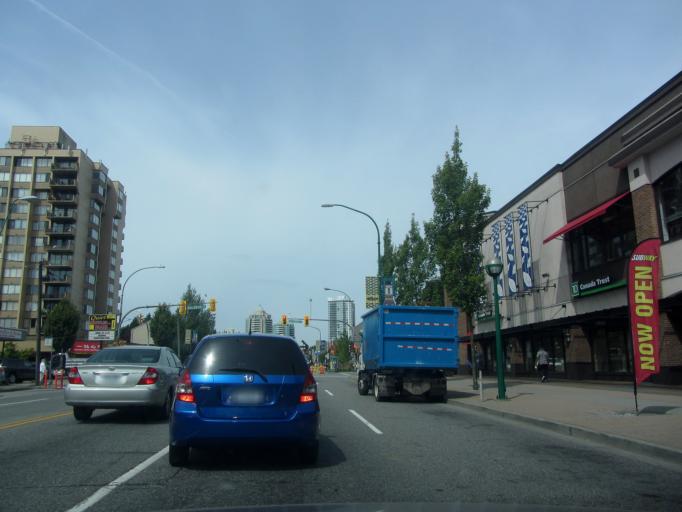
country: CA
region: British Columbia
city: New Westminster
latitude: 49.2183
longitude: -122.9506
